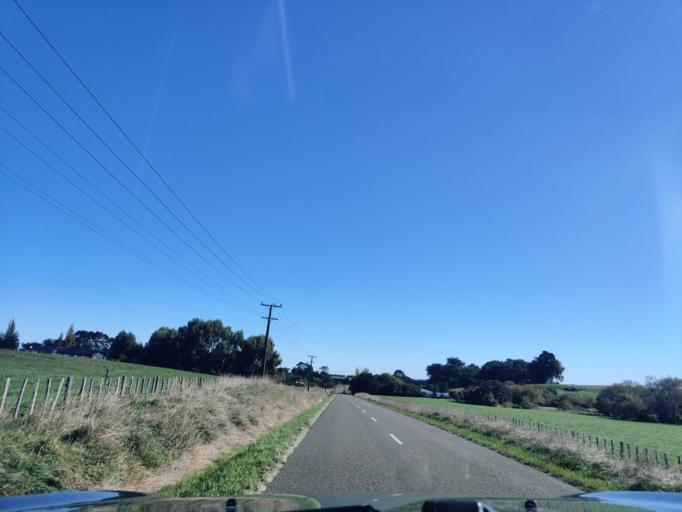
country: NZ
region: Manawatu-Wanganui
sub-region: Palmerston North City
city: Palmerston North
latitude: -40.2412
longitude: 175.6681
